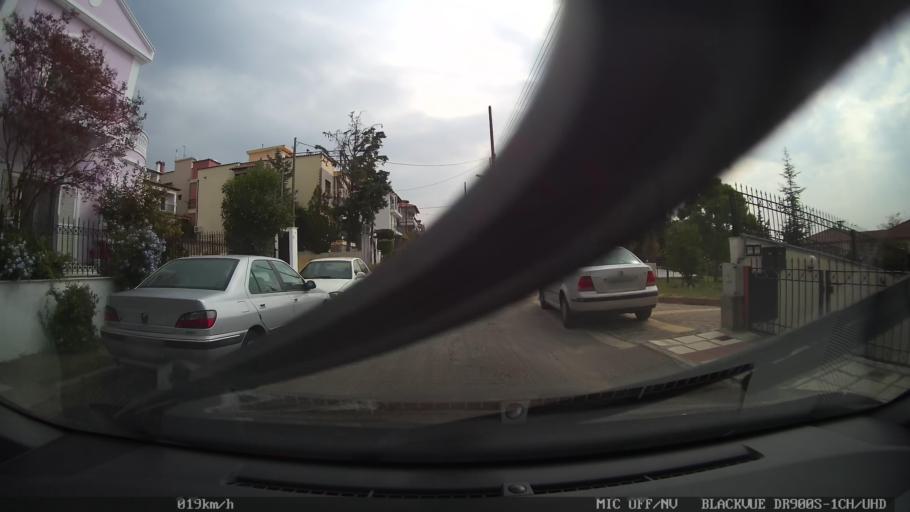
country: GR
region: Central Macedonia
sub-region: Nomos Thessalonikis
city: Pylaia
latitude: 40.6123
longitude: 22.9951
